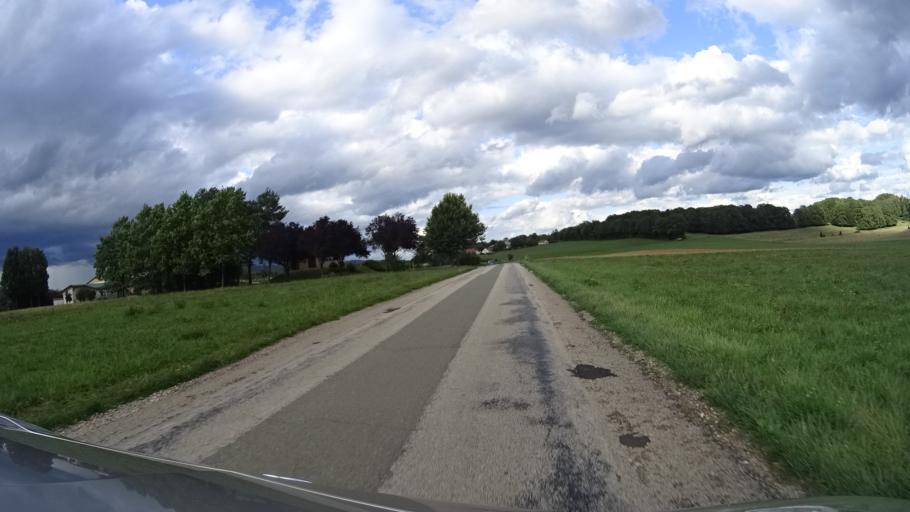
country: FR
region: Franche-Comte
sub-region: Departement du Doubs
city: Nancray
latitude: 47.2378
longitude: 6.1712
